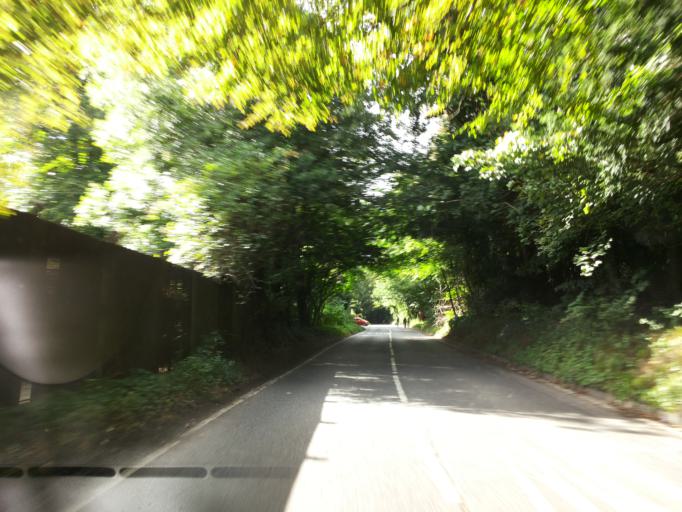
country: GB
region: England
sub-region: Greater London
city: Orpington
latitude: 51.3532
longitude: 0.0758
